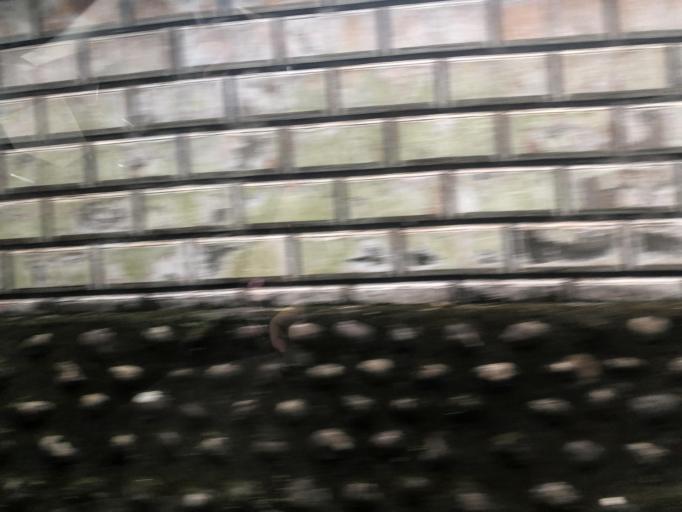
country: TW
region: Taiwan
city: Daxi
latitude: 24.8469
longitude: 121.4488
